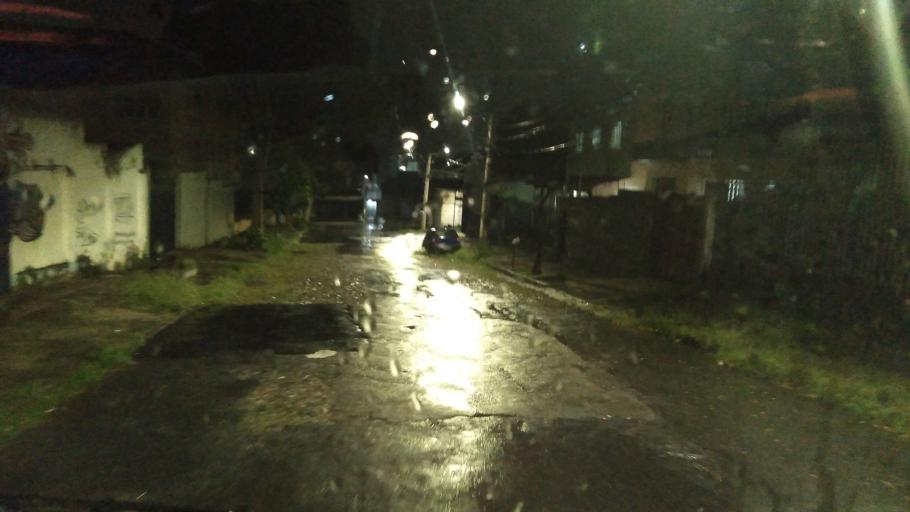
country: BR
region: Minas Gerais
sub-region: Belo Horizonte
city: Belo Horizonte
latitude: -19.9079
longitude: -43.9797
